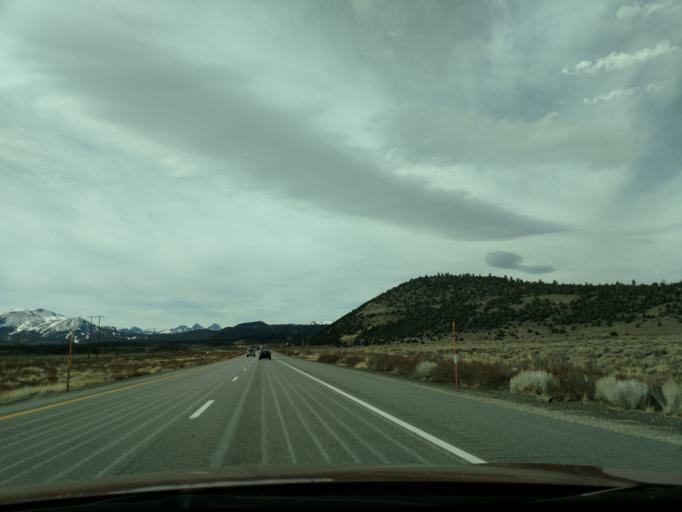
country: US
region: California
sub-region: Mono County
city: Mammoth Lakes
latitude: 37.6338
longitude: -118.8798
